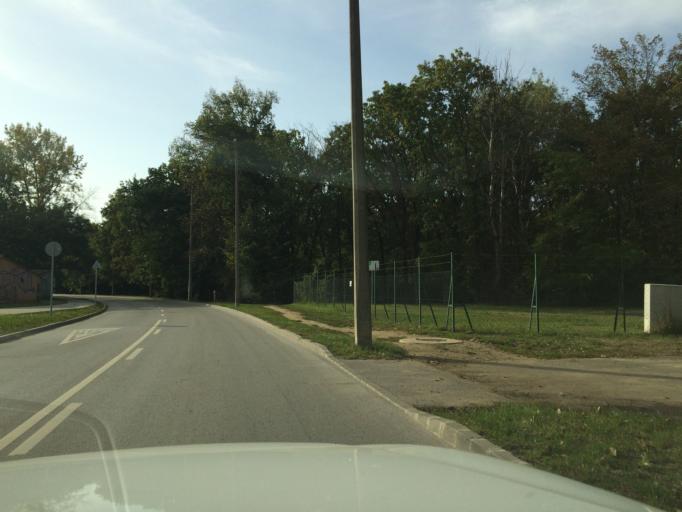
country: HU
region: Szabolcs-Szatmar-Bereg
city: Nyiregyhaza
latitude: 47.9791
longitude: 21.7227
